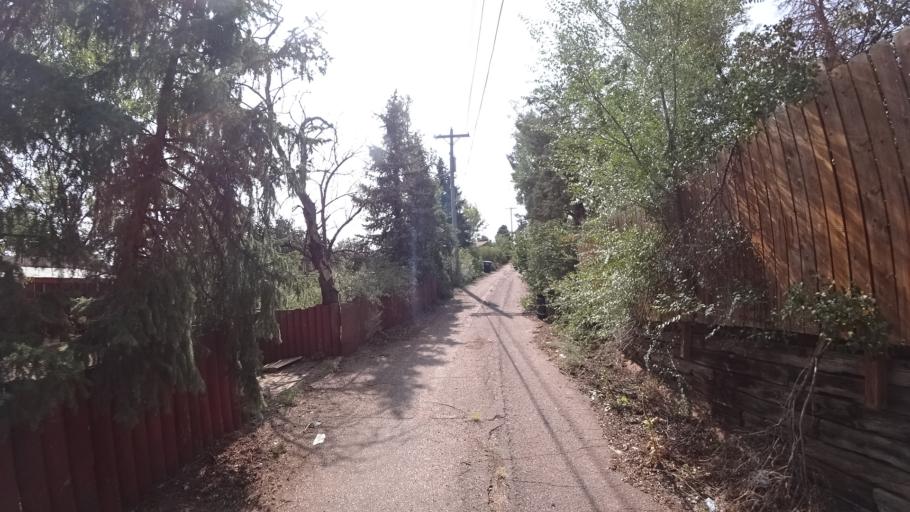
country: US
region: Colorado
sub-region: El Paso County
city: Colorado Springs
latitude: 38.8512
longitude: -104.7897
